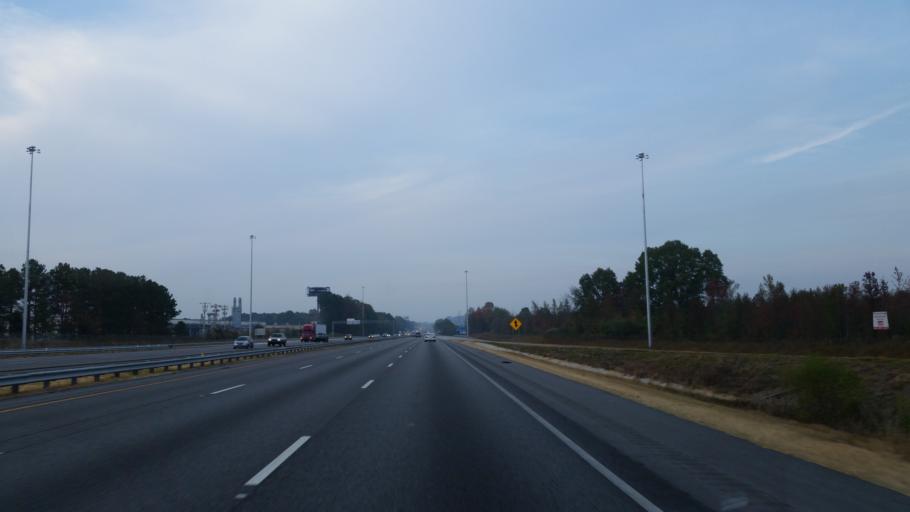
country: US
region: Georgia
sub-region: Gordon County
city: Calhoun
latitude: 34.4450
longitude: -84.9198
